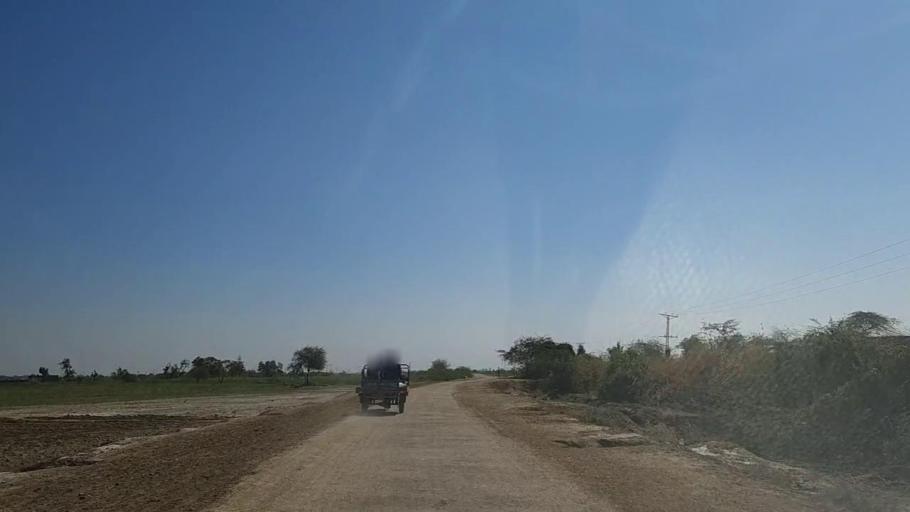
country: PK
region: Sindh
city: Samaro
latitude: 25.3097
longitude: 69.4765
